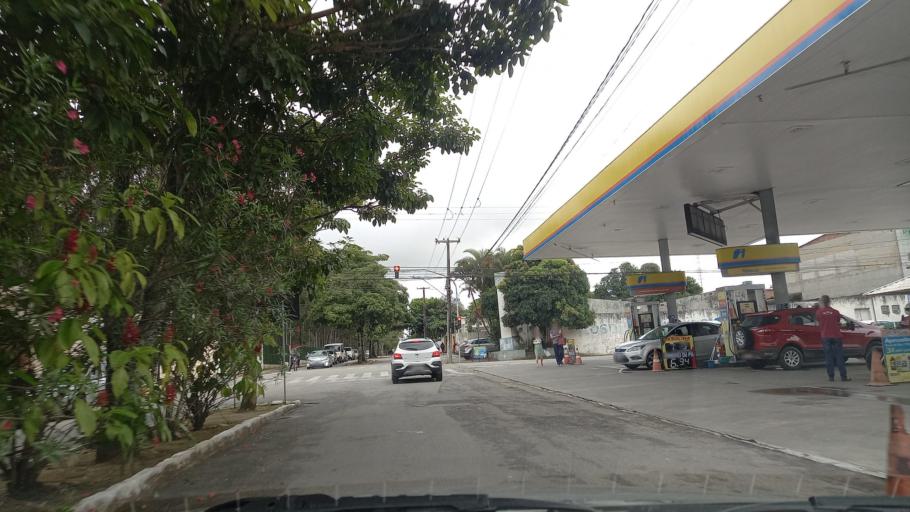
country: BR
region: Pernambuco
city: Garanhuns
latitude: -8.8844
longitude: -36.4830
